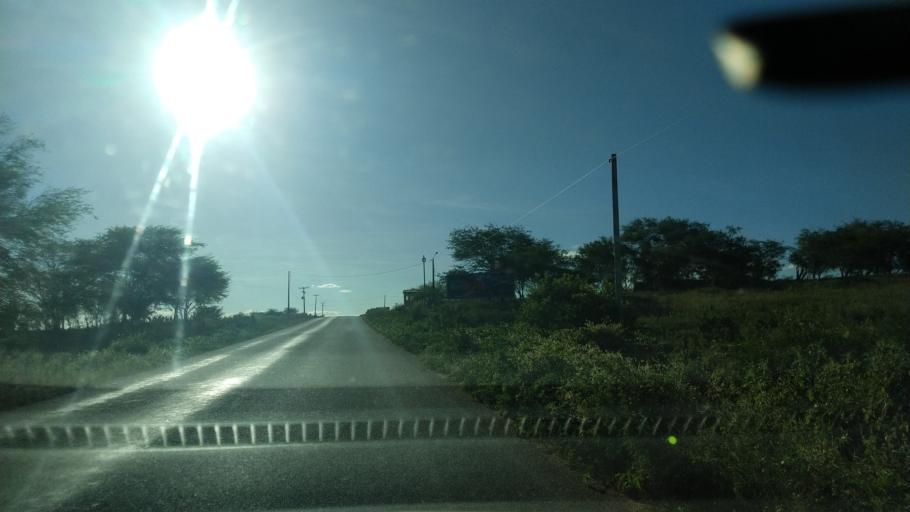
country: BR
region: Rio Grande do Norte
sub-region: Sao Jose Do Campestre
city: Sao Jose do Campestre
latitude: -6.3253
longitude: -35.6995
